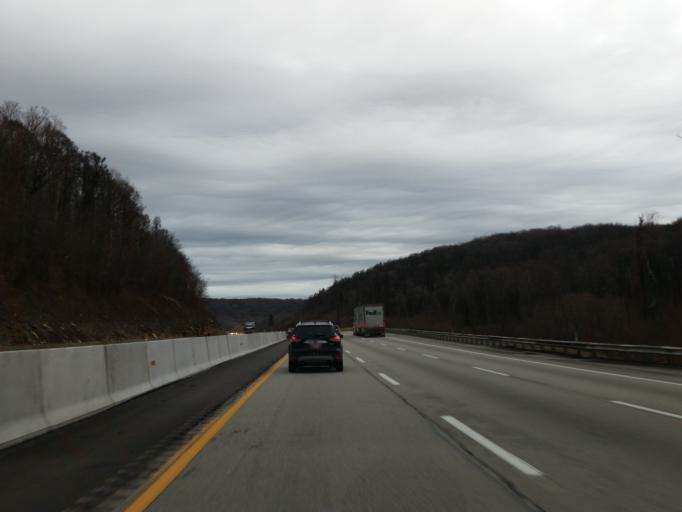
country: US
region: Pennsylvania
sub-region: Westmoreland County
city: Ligonier
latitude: 40.1111
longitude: -79.2471
